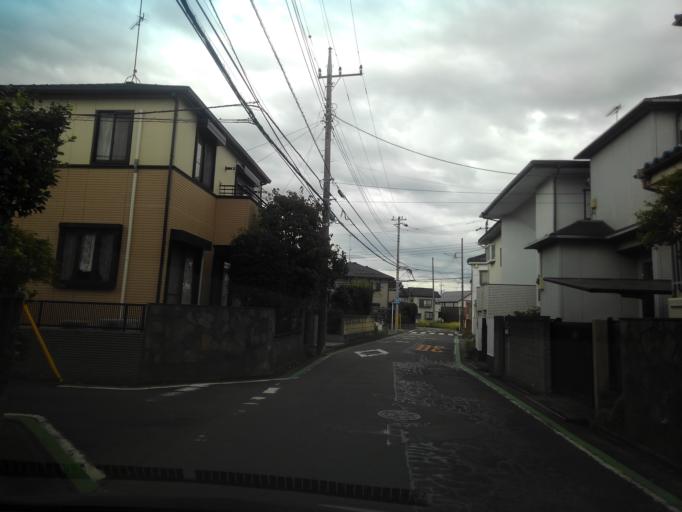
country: JP
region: Saitama
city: Tokorozawa
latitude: 35.7993
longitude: 139.4427
